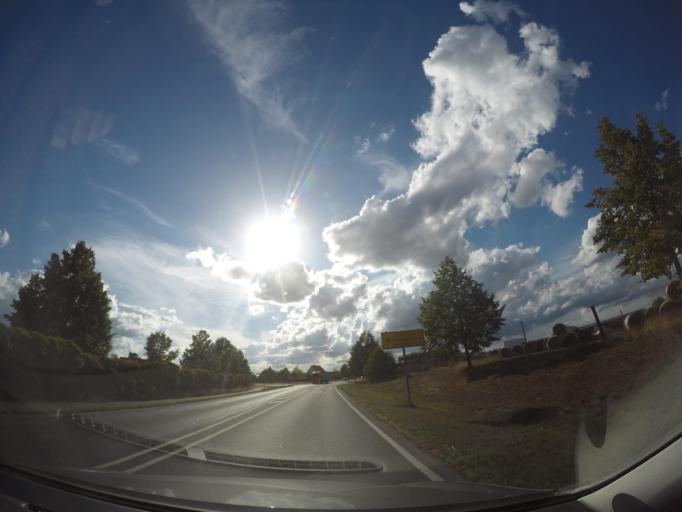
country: DE
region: Saxony-Anhalt
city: Haldensleben I
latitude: 52.3003
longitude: 11.3996
